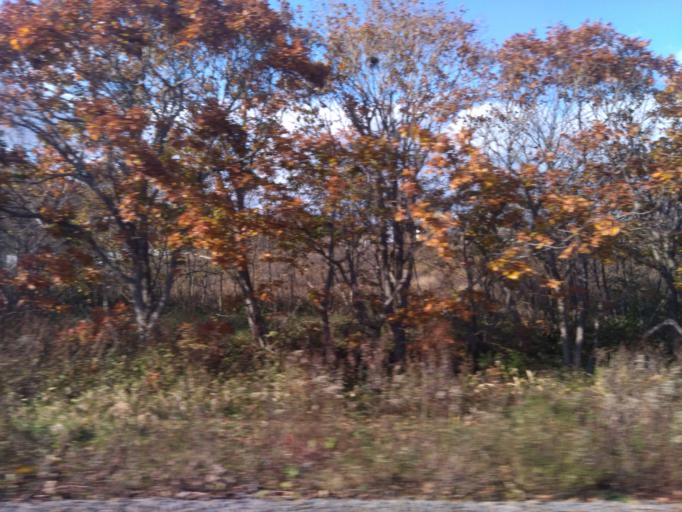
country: JP
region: Hokkaido
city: Shiraoi
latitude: 42.5368
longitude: 141.3307
